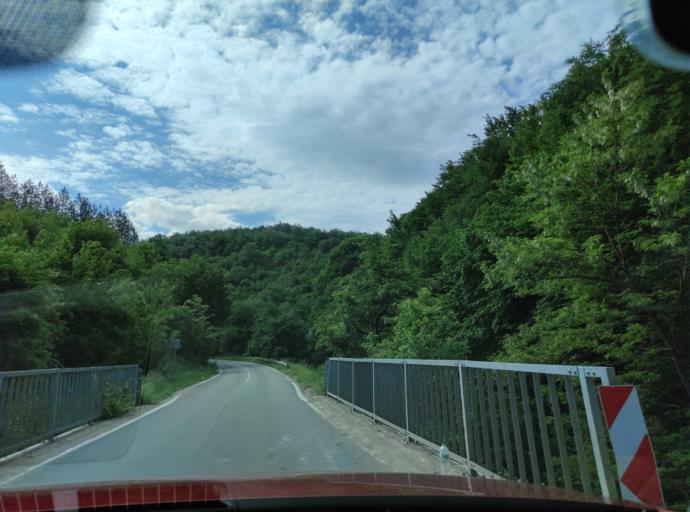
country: BG
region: Montana
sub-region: Obshtina Chiprovtsi
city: Chiprovtsi
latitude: 43.4645
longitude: 22.8806
